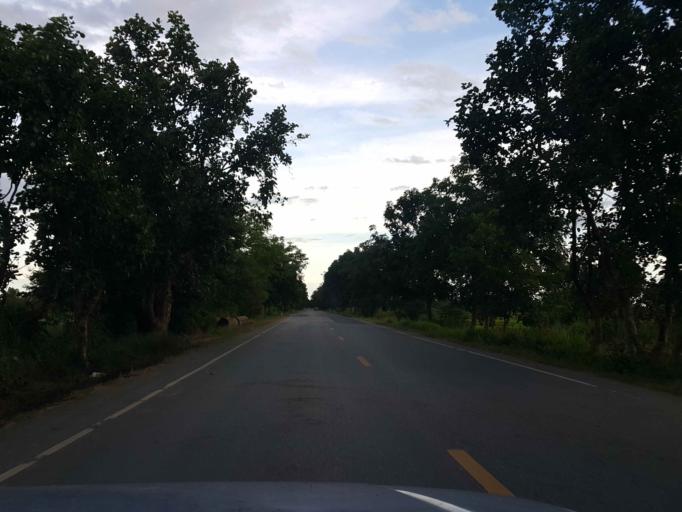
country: TH
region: Sukhothai
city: Sawankhalok
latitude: 17.3788
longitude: 99.7380
